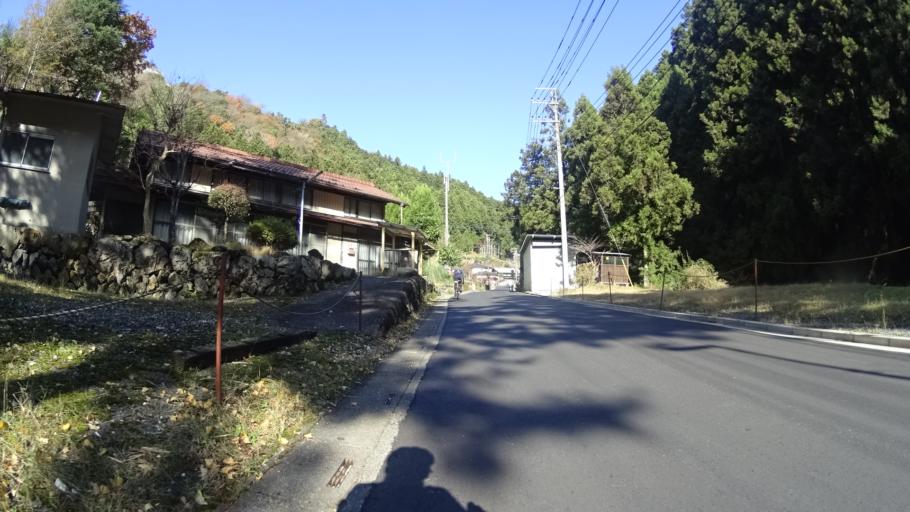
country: JP
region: Saitama
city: Chichibu
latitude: 35.9166
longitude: 139.1503
